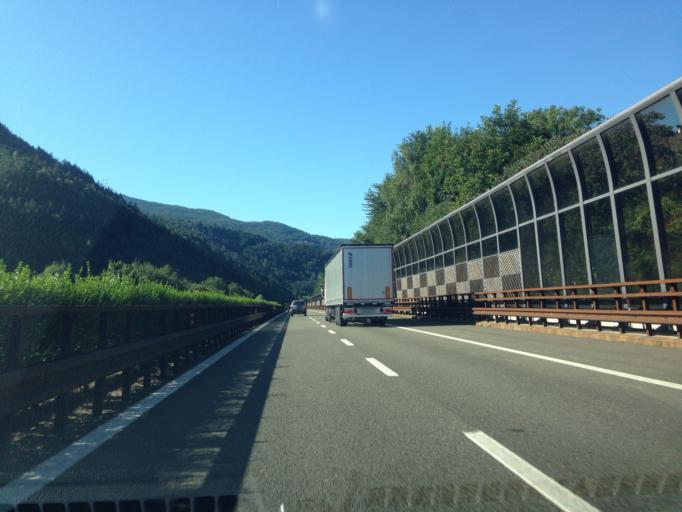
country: IT
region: Trentino-Alto Adige
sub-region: Bolzano
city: Velturno
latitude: 46.6689
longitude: 11.6157
